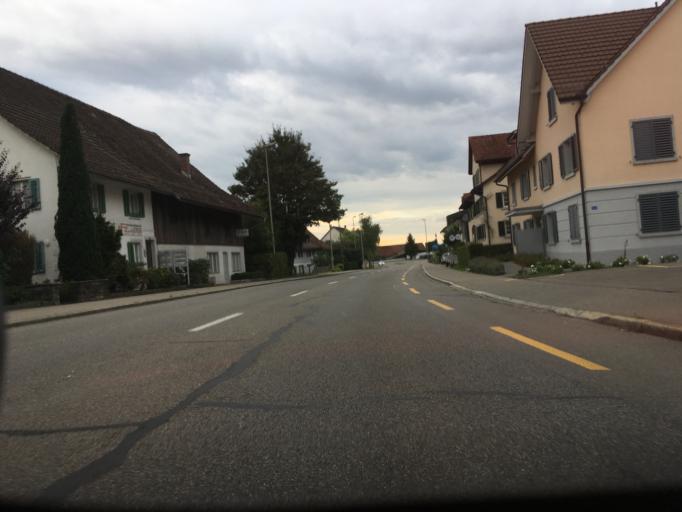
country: CH
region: Zurich
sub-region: Bezirk Uster
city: Hegnau
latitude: 47.3897
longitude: 8.6734
